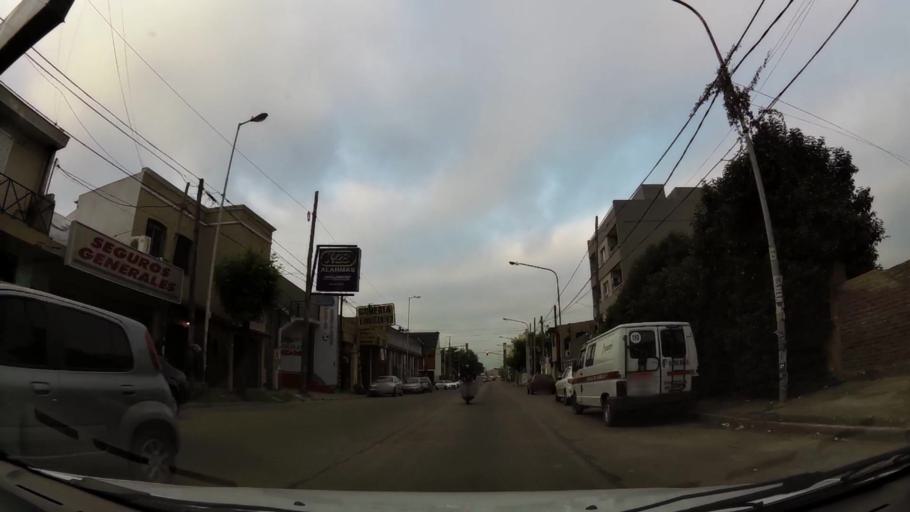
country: AR
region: Buenos Aires
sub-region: Partido de Moron
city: Moron
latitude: -34.6524
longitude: -58.5853
